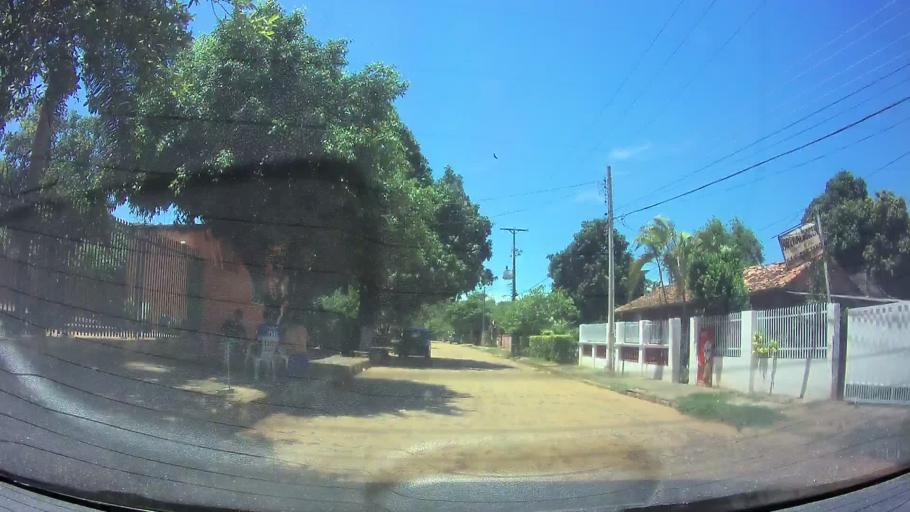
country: PY
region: Central
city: Limpio
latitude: -25.2436
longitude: -57.4871
